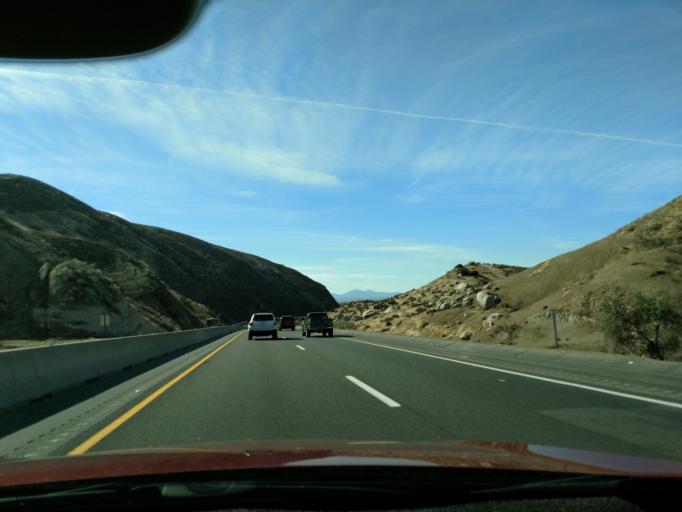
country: US
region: California
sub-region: Riverside County
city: Beaumont
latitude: 33.8705
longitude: -116.9967
